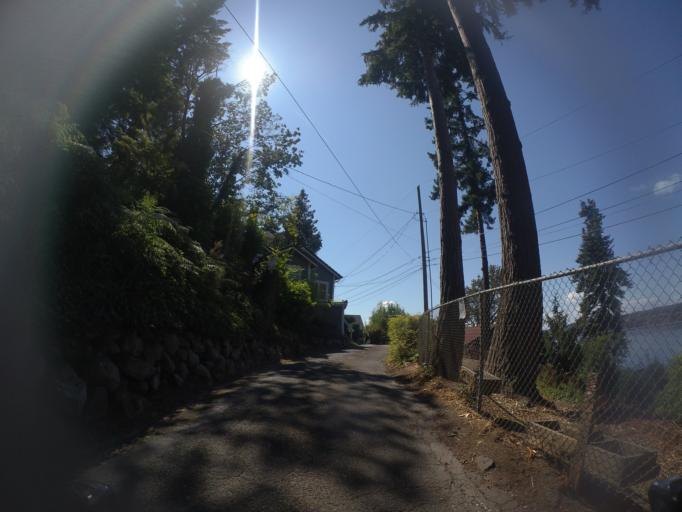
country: US
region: Washington
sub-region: Pierce County
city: University Place
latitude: 47.2185
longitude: -122.5693
